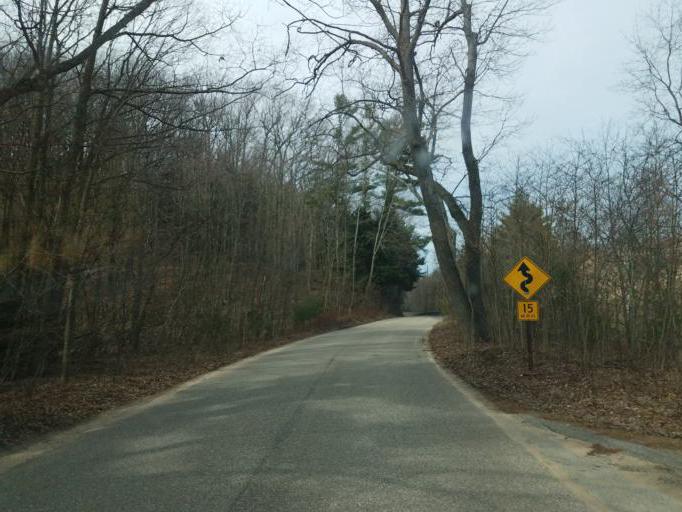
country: US
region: Michigan
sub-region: Oceana County
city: Hart
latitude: 43.6571
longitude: -86.5296
